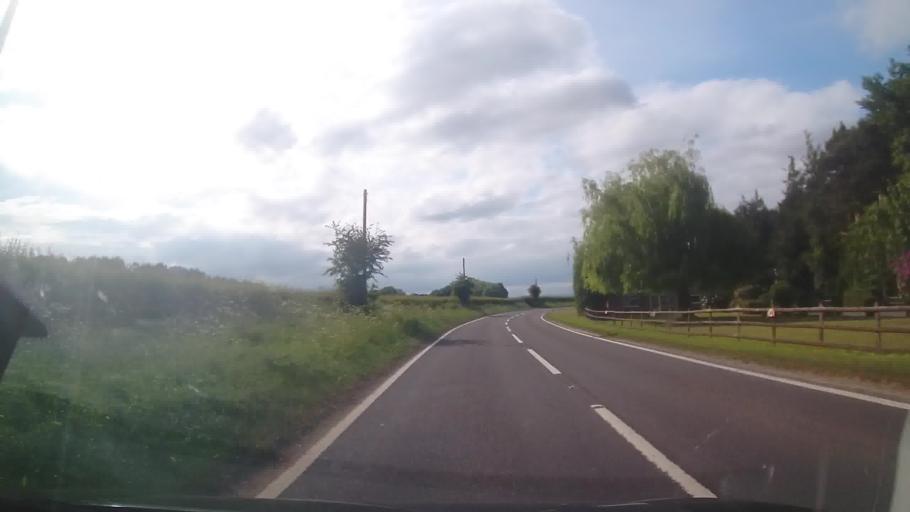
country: GB
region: England
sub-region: Shropshire
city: Clive
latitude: 52.8029
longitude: -2.7735
